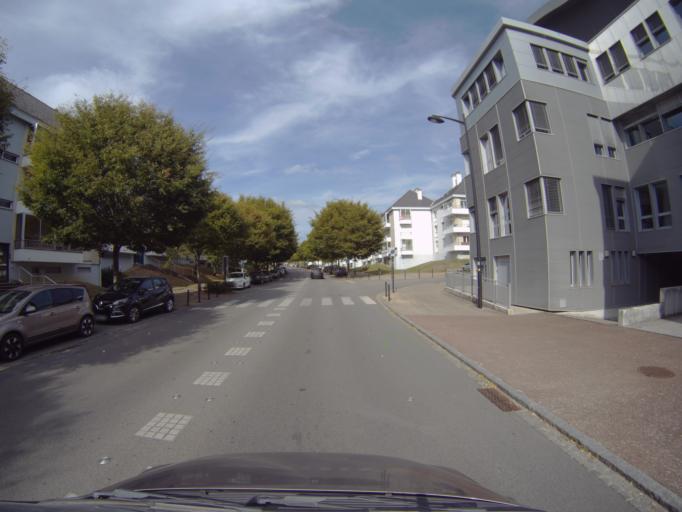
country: FR
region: Pays de la Loire
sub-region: Departement de la Loire-Atlantique
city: Saint-Herblain
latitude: 47.2115
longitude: -1.6487
